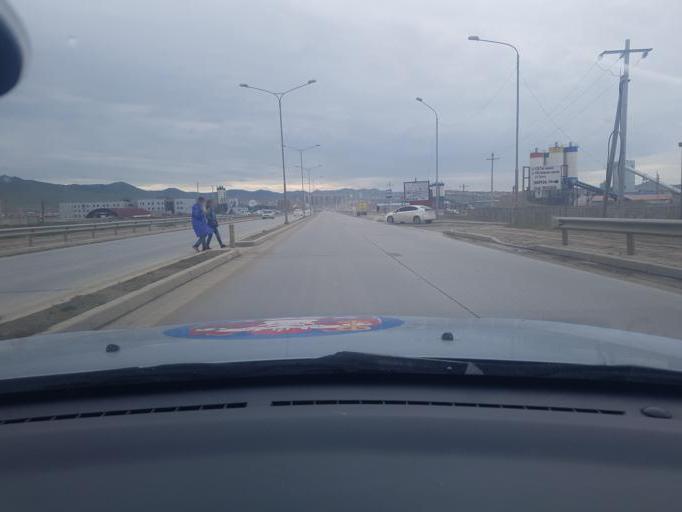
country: MN
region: Ulaanbaatar
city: Ulaanbaatar
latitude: 47.8877
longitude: 106.7852
